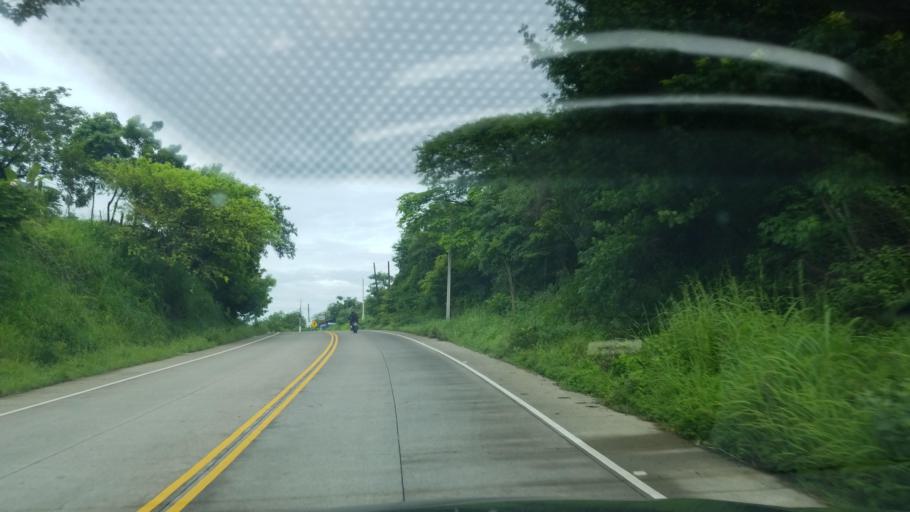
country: HN
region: Choluteca
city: Pespire
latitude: 13.6697
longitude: -87.3578
